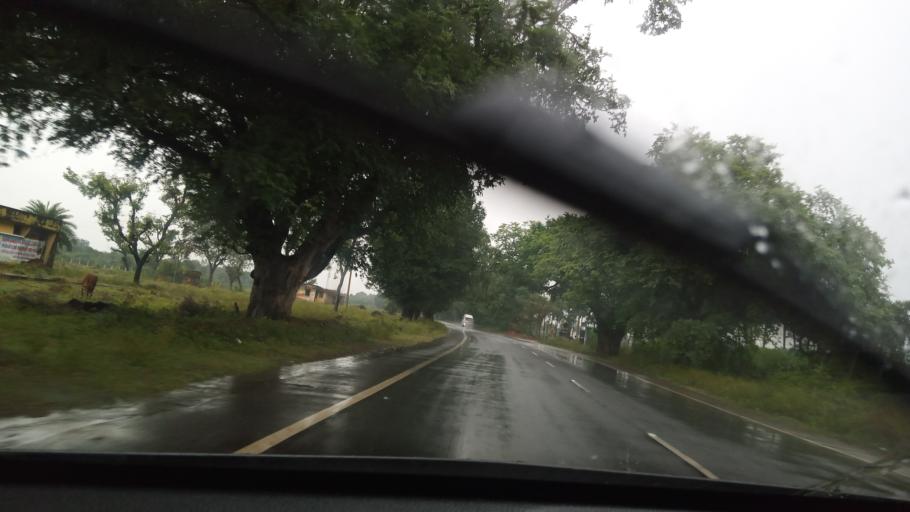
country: IN
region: Tamil Nadu
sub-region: Vellore
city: Kalavai
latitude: 12.8050
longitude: 79.4245
